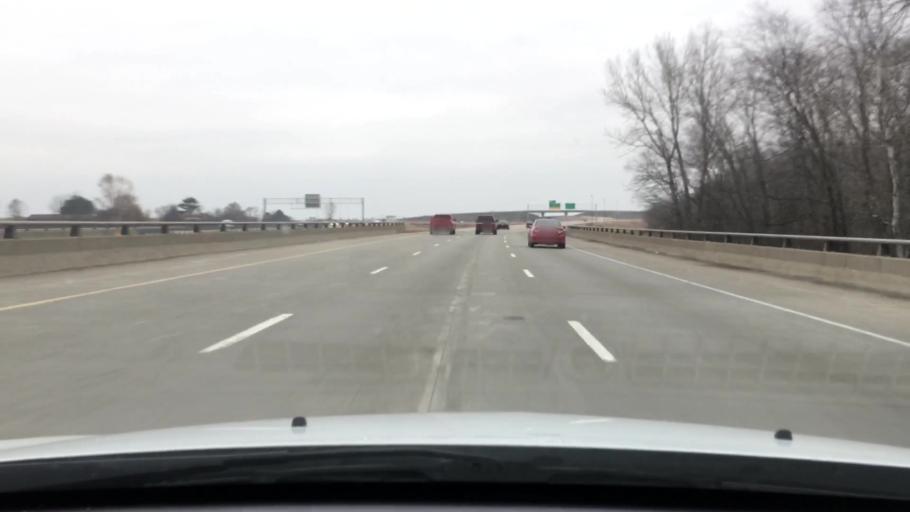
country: US
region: Illinois
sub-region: Logan County
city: Lincoln
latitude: 40.1685
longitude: -89.4176
